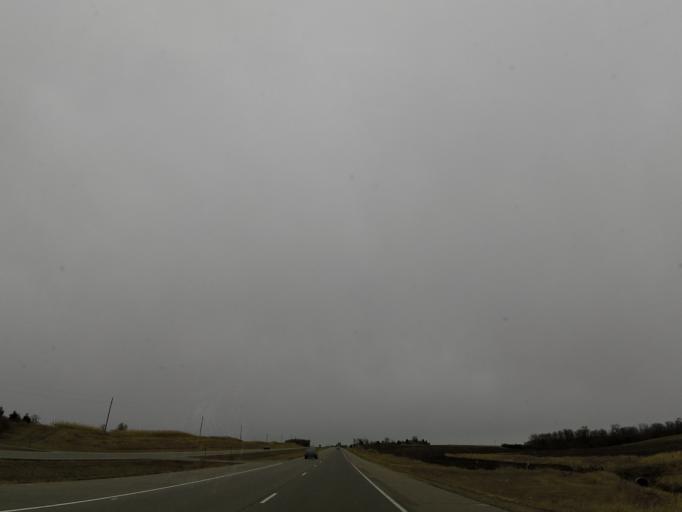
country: US
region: Minnesota
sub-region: Le Sueur County
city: Le Sueur
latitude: 44.5223
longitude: -93.8464
